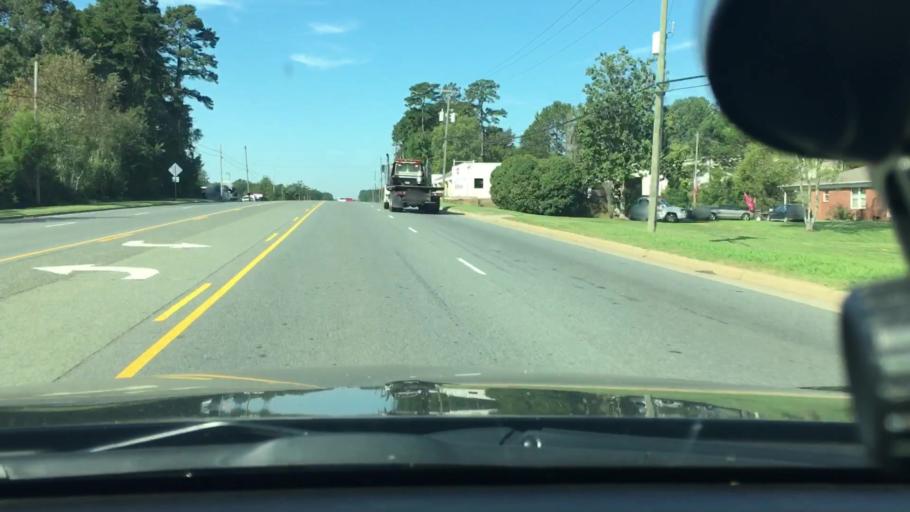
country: US
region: North Carolina
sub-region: Cabarrus County
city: Midland
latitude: 35.2493
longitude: -80.5503
